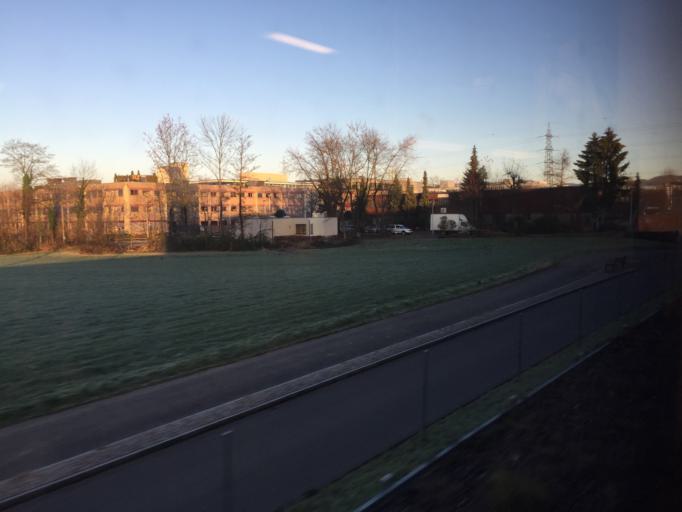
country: CH
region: Zug
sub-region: Zug
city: Zug
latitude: 47.1857
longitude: 8.5173
